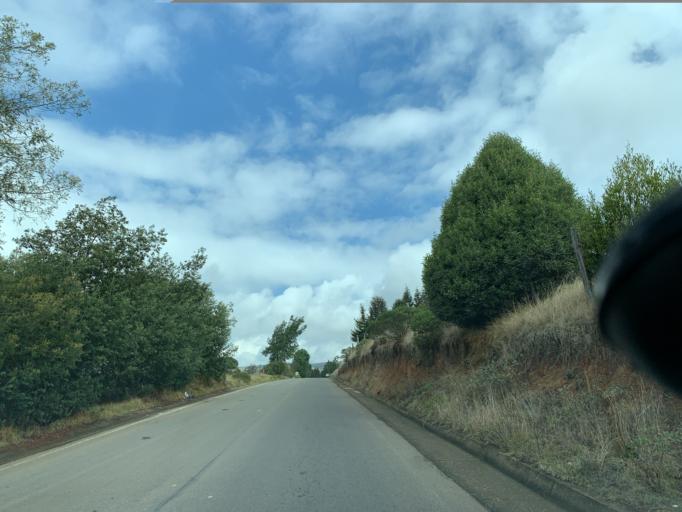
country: CO
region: Boyaca
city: Tunja
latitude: 5.5692
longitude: -73.3632
